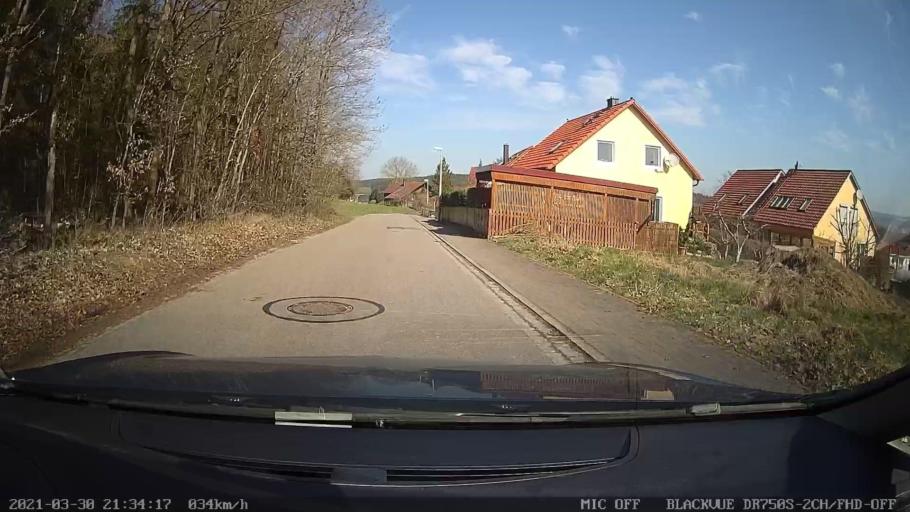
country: DE
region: Bavaria
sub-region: Upper Palatinate
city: Zeitlarn
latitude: 49.0966
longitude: 12.1005
